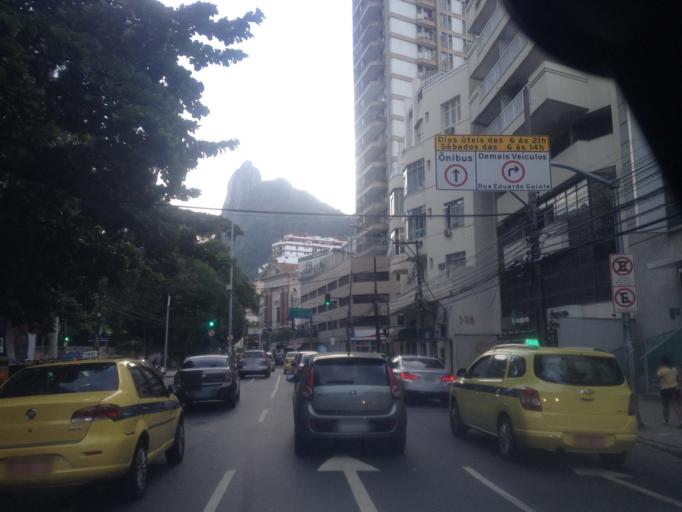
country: BR
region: Rio de Janeiro
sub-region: Rio De Janeiro
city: Rio de Janeiro
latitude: -22.9495
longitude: -43.1882
